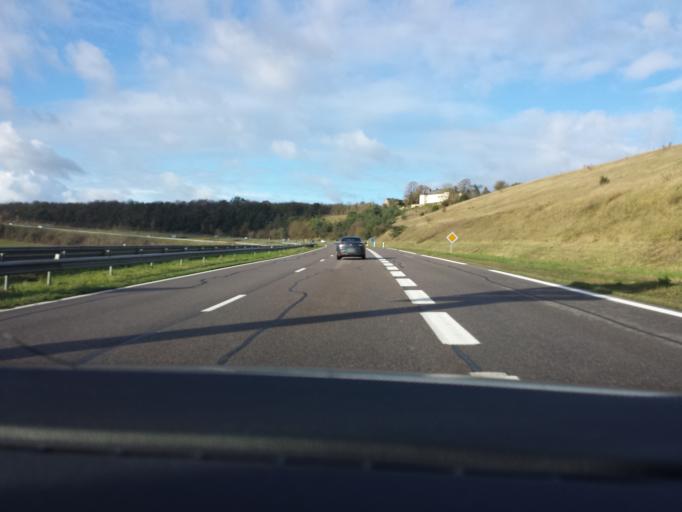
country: FR
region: Haute-Normandie
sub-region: Departement de l'Eure
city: Menilles
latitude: 49.0130
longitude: 1.3510
